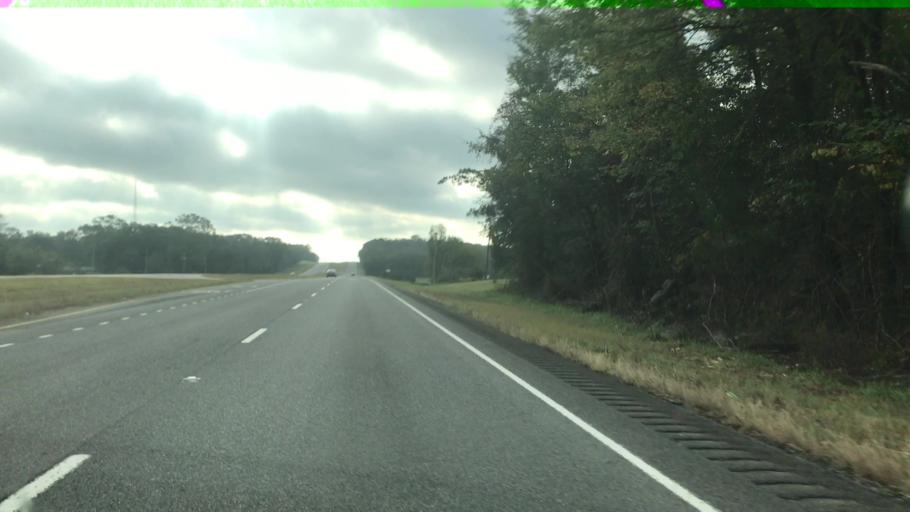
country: US
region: Alabama
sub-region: Morgan County
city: Danville
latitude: 34.4027
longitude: -87.1361
